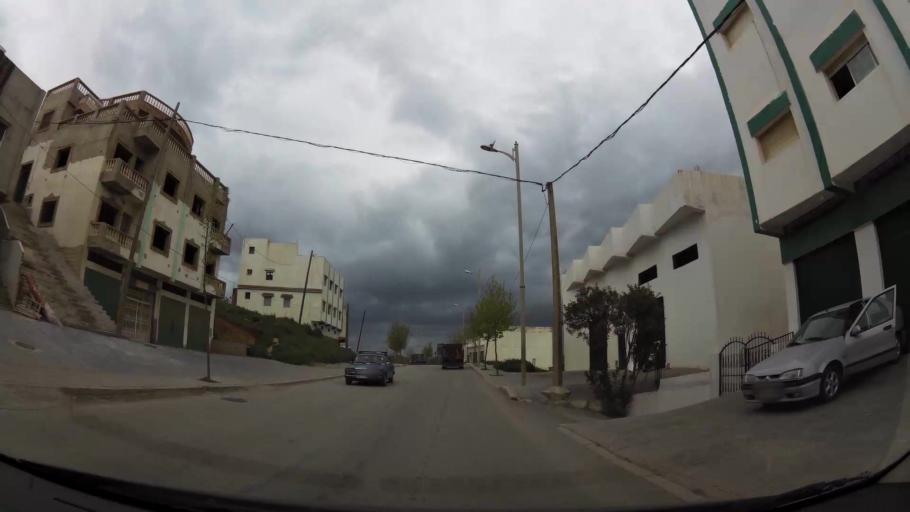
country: MA
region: Tanger-Tetouan
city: Tetouan
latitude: 35.5562
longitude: -5.3915
